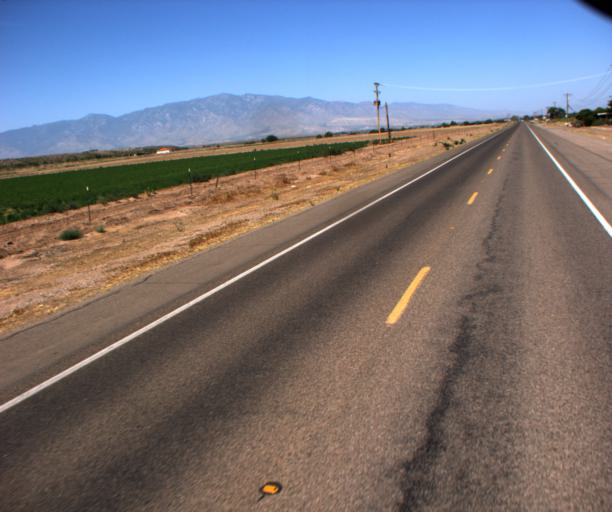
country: US
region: Arizona
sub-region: Graham County
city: Safford
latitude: 32.8128
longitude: -109.6055
